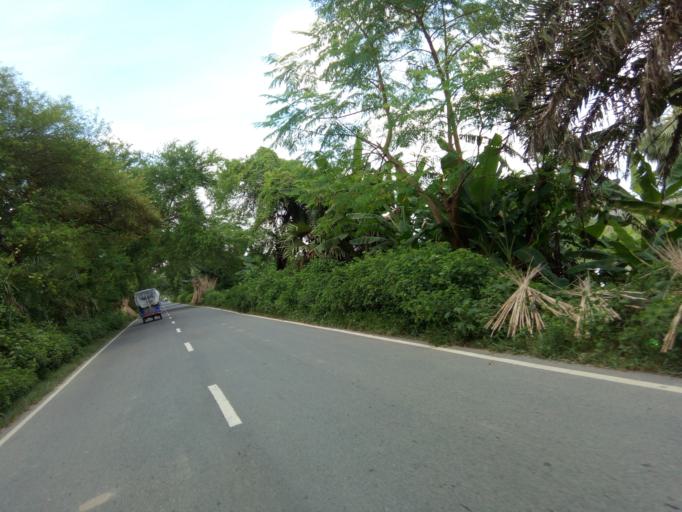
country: BD
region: Dhaka
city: Tungipara
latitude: 22.9614
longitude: 89.8177
